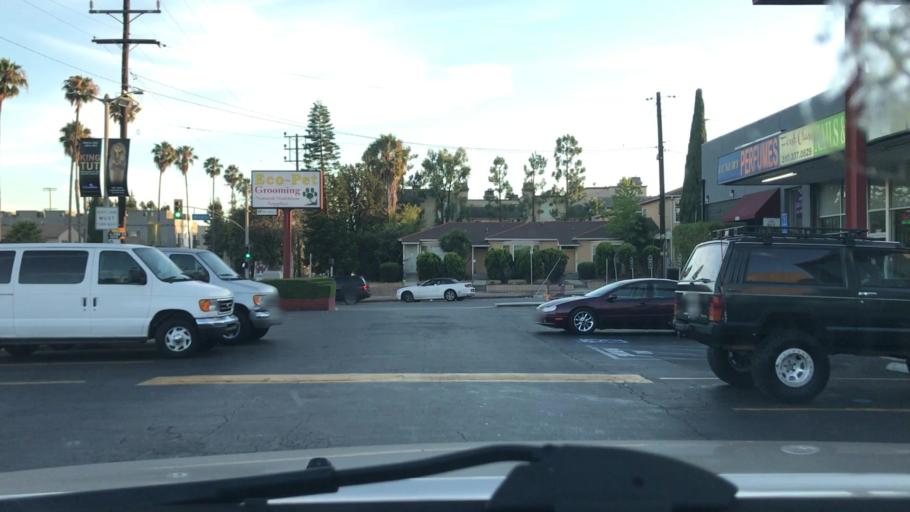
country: US
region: California
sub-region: Los Angeles County
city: Ladera Heights
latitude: 33.9755
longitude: -118.3742
